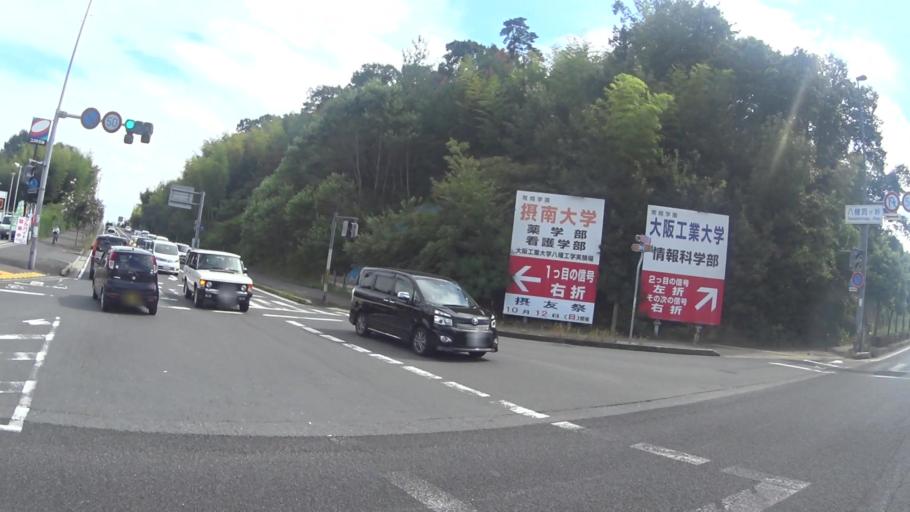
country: JP
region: Kyoto
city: Yawata
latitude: 34.8526
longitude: 135.7045
